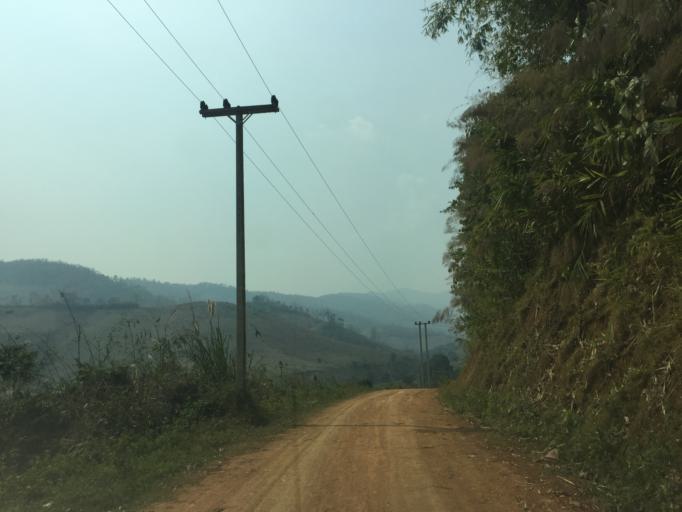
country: TH
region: Phayao
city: Phu Sang
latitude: 19.5784
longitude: 100.5276
